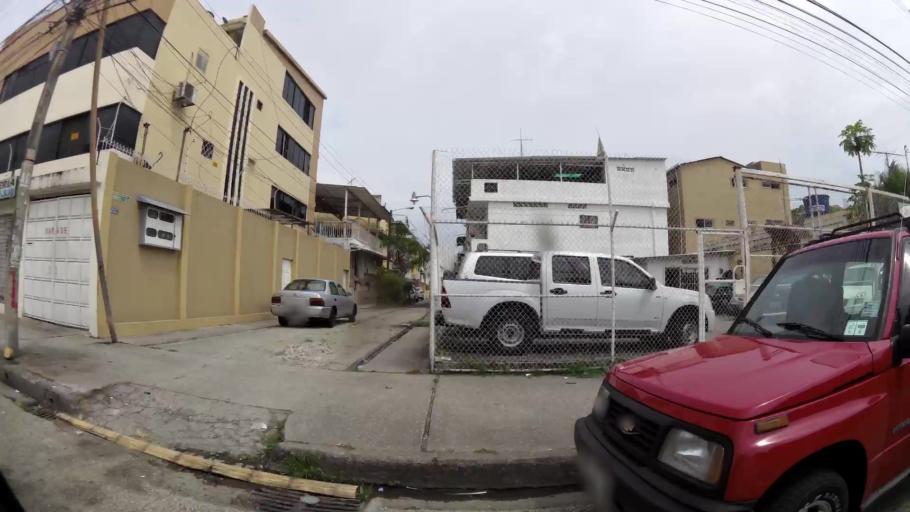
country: EC
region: Guayas
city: Eloy Alfaro
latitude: -2.1496
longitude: -79.8948
